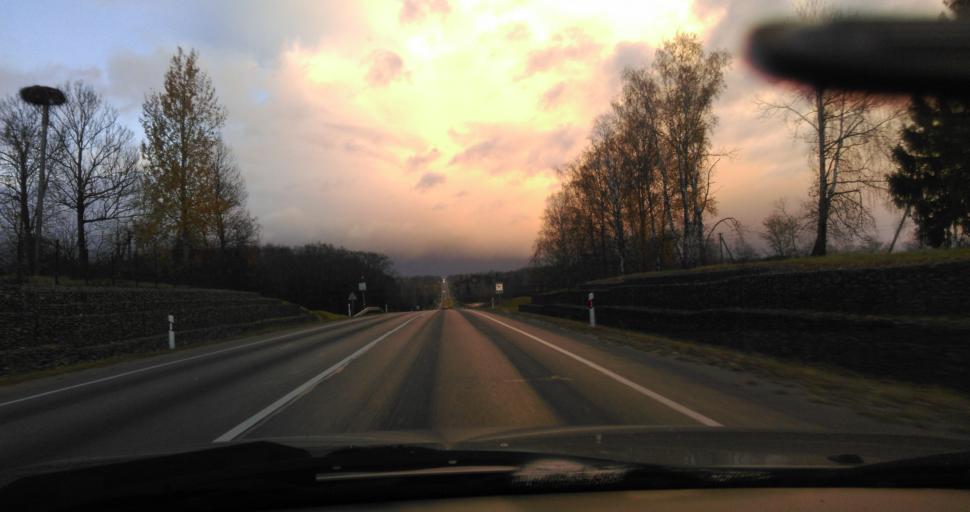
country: LT
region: Utenos apskritis
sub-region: Utena
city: Utena
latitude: 55.5135
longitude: 25.6453
